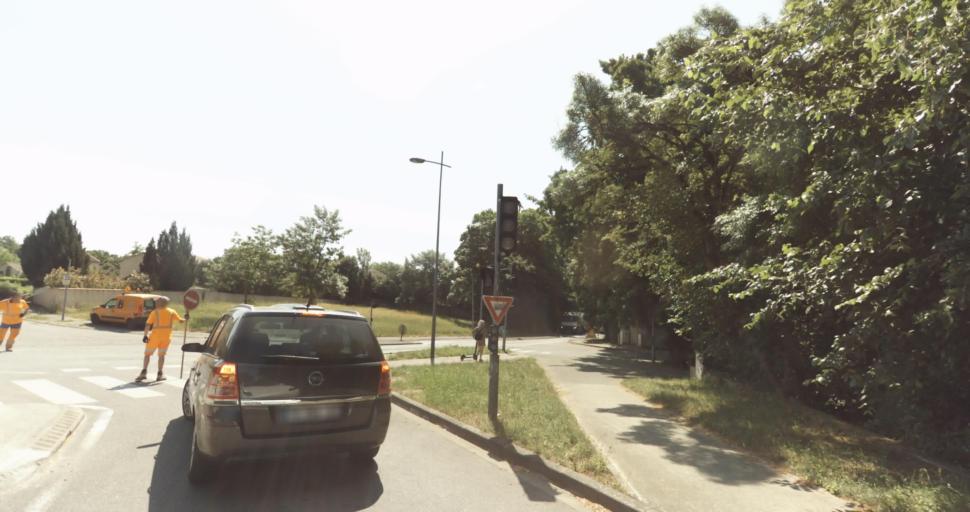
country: FR
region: Midi-Pyrenees
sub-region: Departement de la Haute-Garonne
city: Plaisance-du-Touch
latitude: 43.5751
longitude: 1.2908
